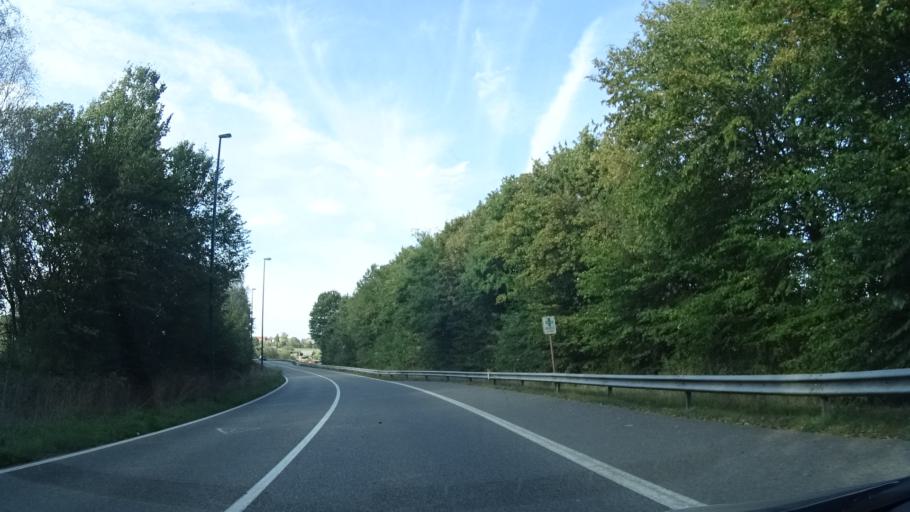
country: BE
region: Wallonia
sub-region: Province de Namur
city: Cerfontaine
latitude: 50.2197
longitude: 4.3834
